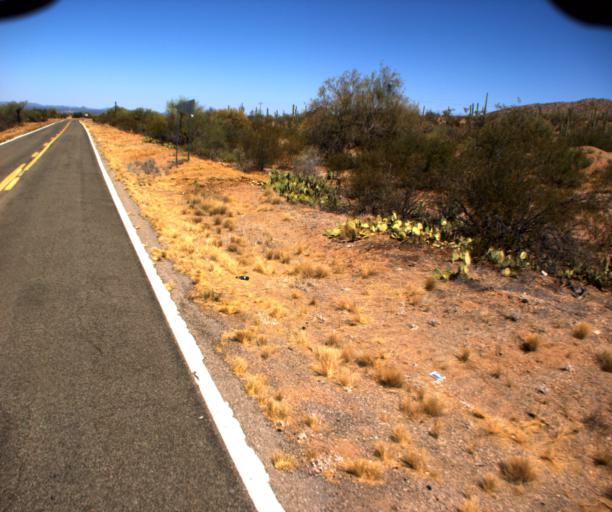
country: US
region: Arizona
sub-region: Pima County
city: Sells
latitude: 32.1746
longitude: -112.2235
